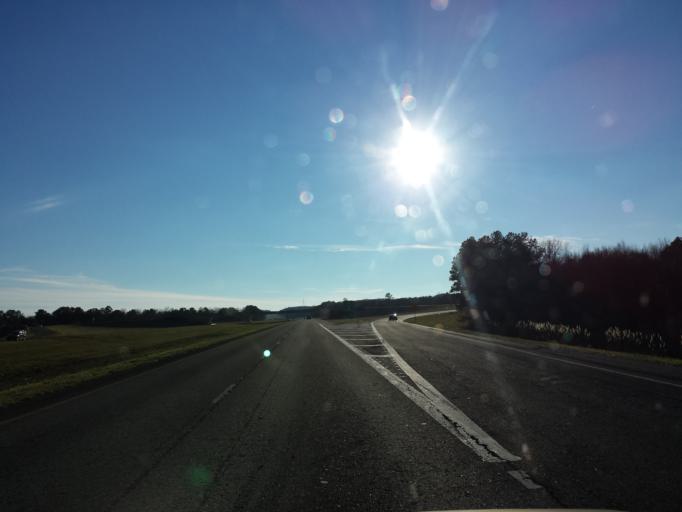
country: US
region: Alabama
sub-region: Hale County
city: Moundville
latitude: 33.0934
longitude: -87.6731
